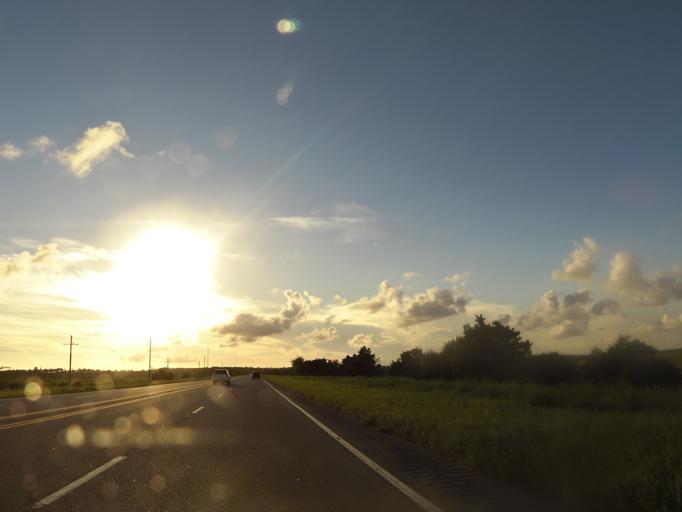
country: US
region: Georgia
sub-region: Glynn County
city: Brunswick
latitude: 31.1103
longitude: -81.5183
